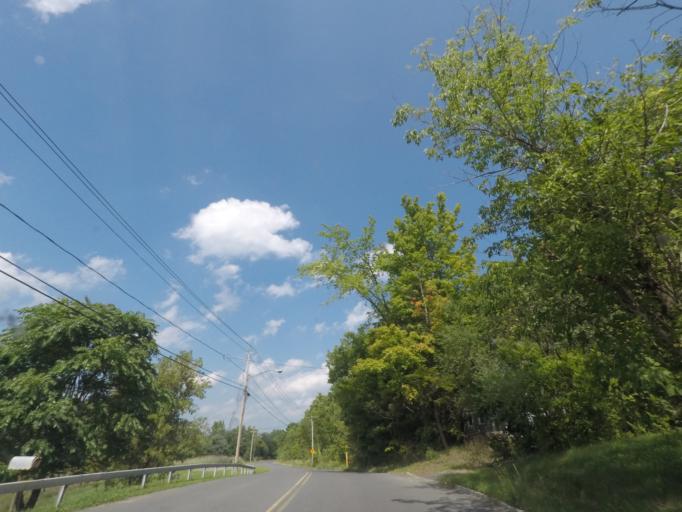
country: US
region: New York
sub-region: Saratoga County
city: Waterford
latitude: 42.7813
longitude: -73.6613
